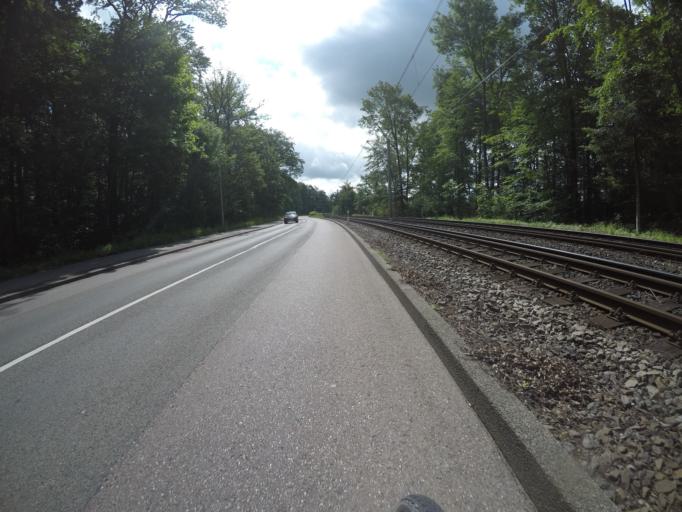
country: DE
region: Baden-Wuerttemberg
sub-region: Regierungsbezirk Stuttgart
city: Stuttgart-Ost
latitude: 48.7492
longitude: 9.2040
